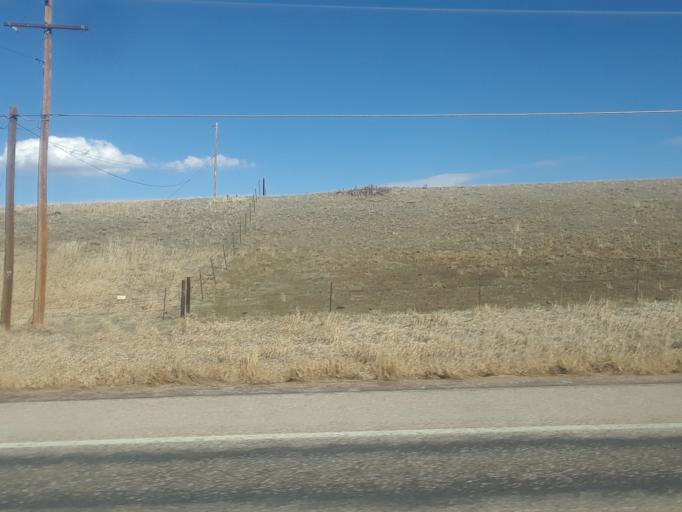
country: US
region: Colorado
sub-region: Boulder County
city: Boulder
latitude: 40.1178
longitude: -105.2823
